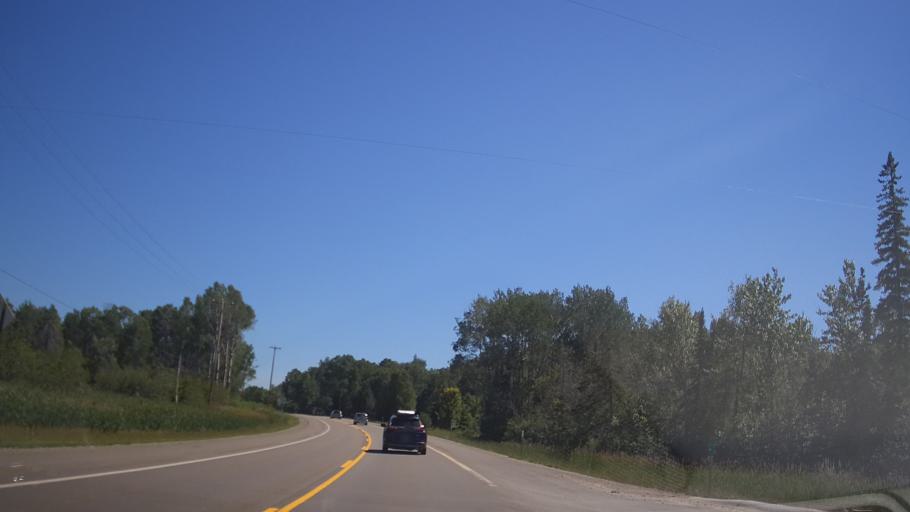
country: US
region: Michigan
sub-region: Mackinac County
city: Saint Ignace
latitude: 45.6230
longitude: -84.7821
